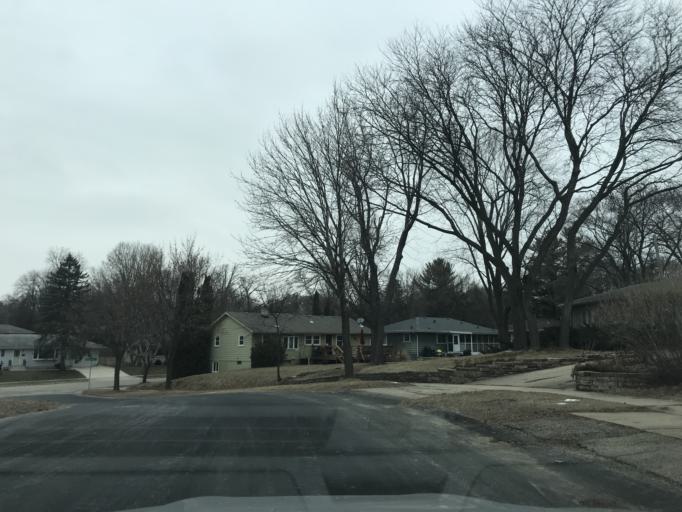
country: US
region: Wisconsin
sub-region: Dane County
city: Monona
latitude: 43.0876
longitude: -89.2990
